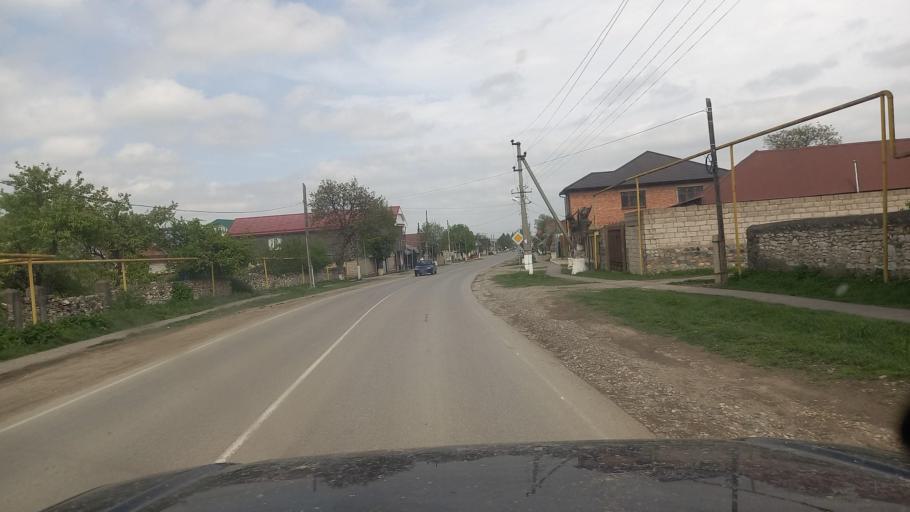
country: RU
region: Kabardino-Balkariya
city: Sarmakovo
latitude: 43.7380
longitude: 43.1826
